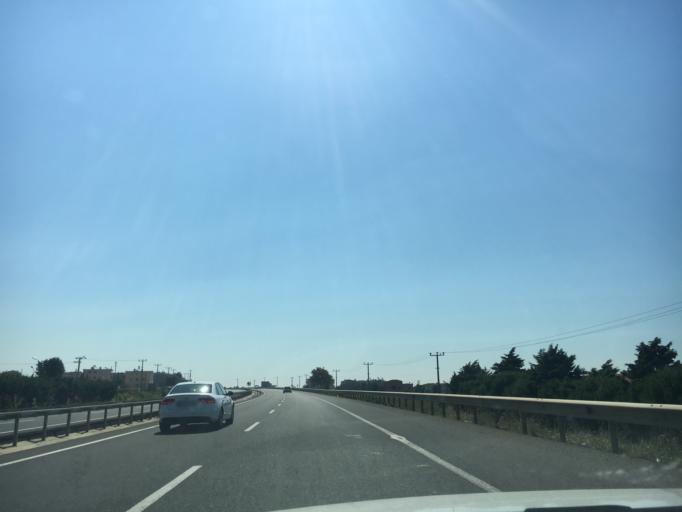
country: TR
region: Tekirdag
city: Marmara Ereglisi
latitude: 40.9707
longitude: 27.8845
